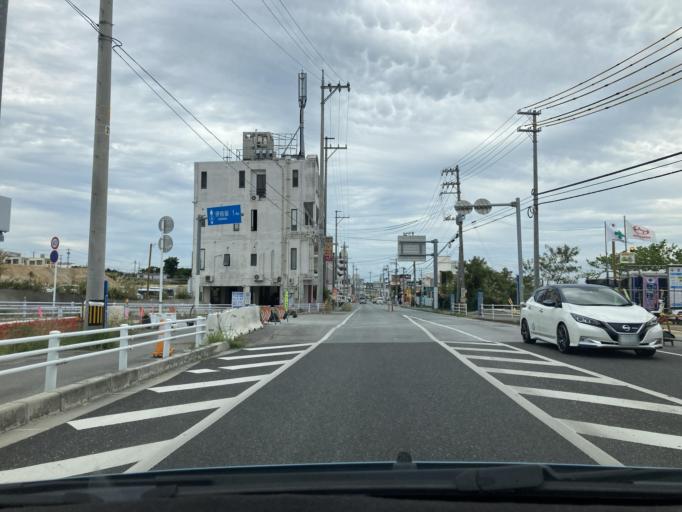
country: JP
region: Okinawa
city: Okinawa
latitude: 26.3826
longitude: 127.7458
